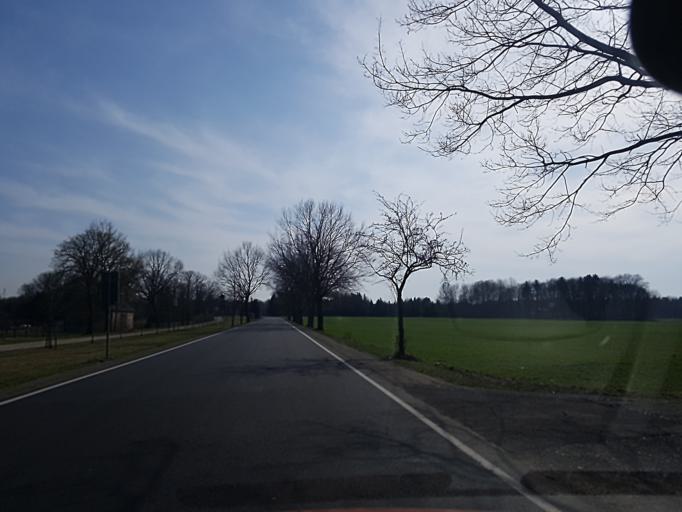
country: DE
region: Brandenburg
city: Bronkow
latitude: 51.6723
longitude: 13.9135
